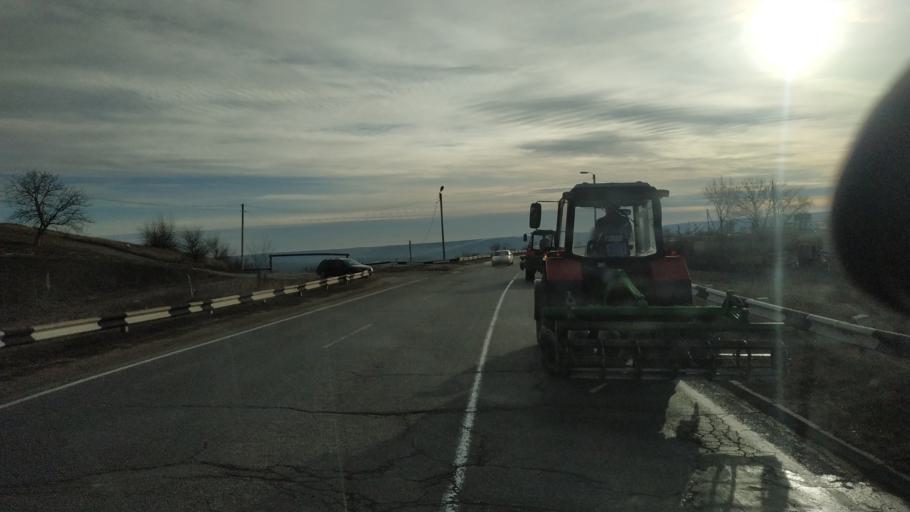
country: MD
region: Chisinau
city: Vadul lui Voda
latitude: 47.0896
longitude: 29.0672
